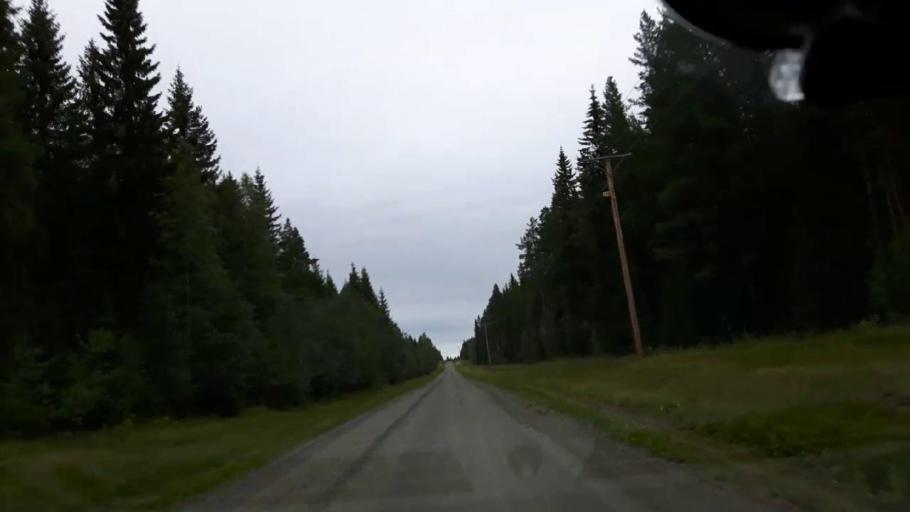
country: SE
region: Vaesternorrland
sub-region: Ange Kommun
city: Fransta
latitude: 62.8016
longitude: 16.0236
